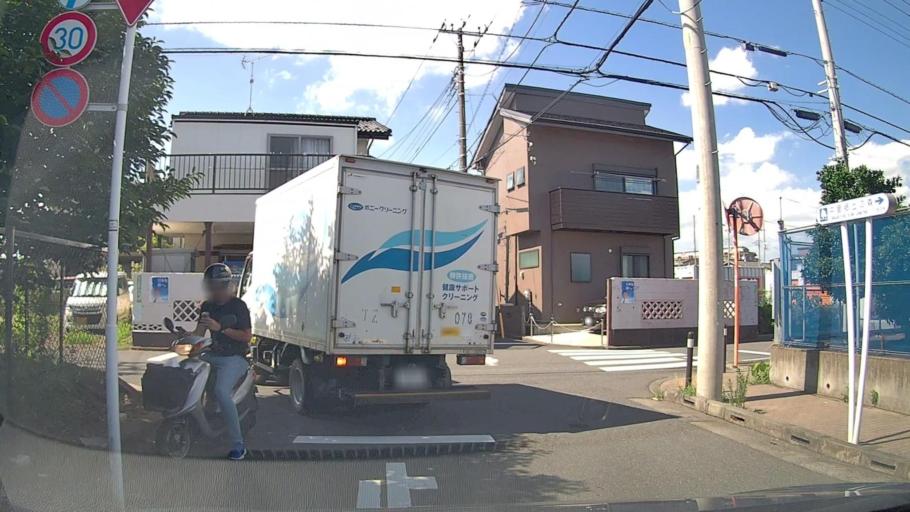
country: JP
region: Saitama
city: Wako
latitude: 35.7696
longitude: 139.6033
